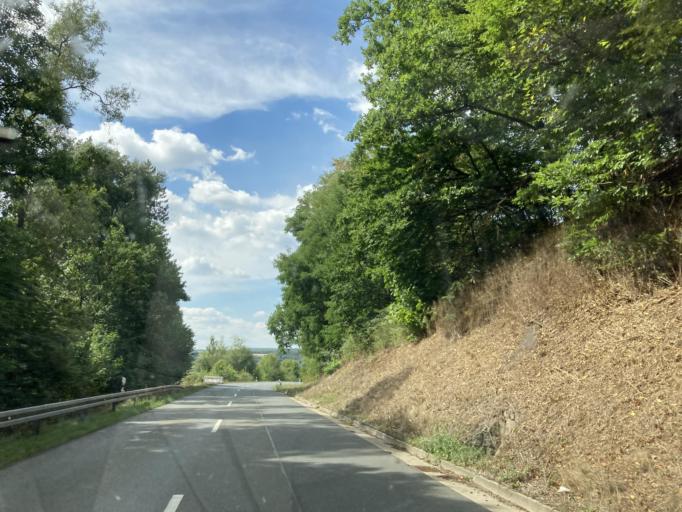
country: DE
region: Bavaria
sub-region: Upper Franconia
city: Kupferberg
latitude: 50.1419
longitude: 11.5490
